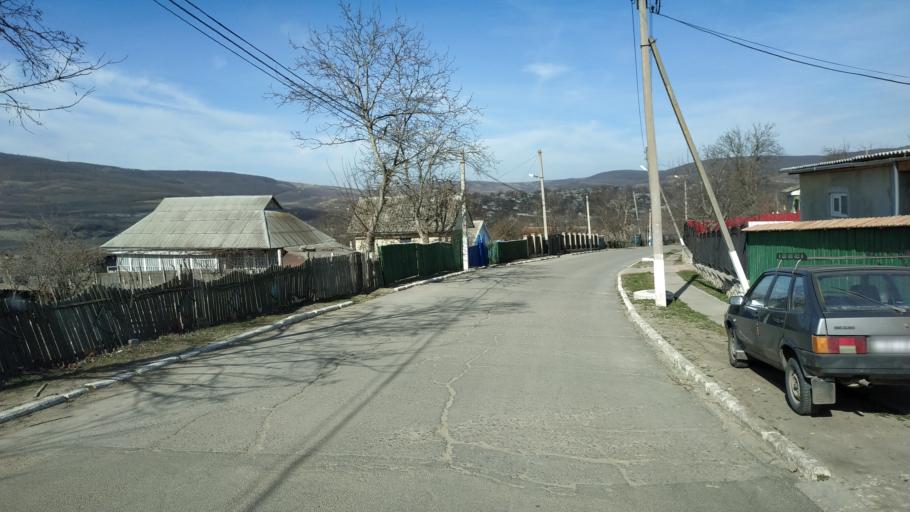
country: MD
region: Nisporeni
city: Nisporeni
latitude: 47.0726
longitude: 28.2615
